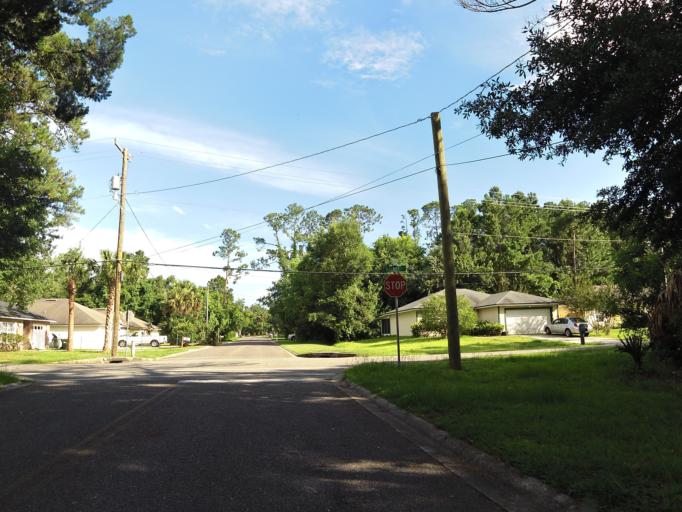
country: US
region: Florida
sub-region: Clay County
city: Green Cove Springs
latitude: 29.9898
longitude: -81.6943
